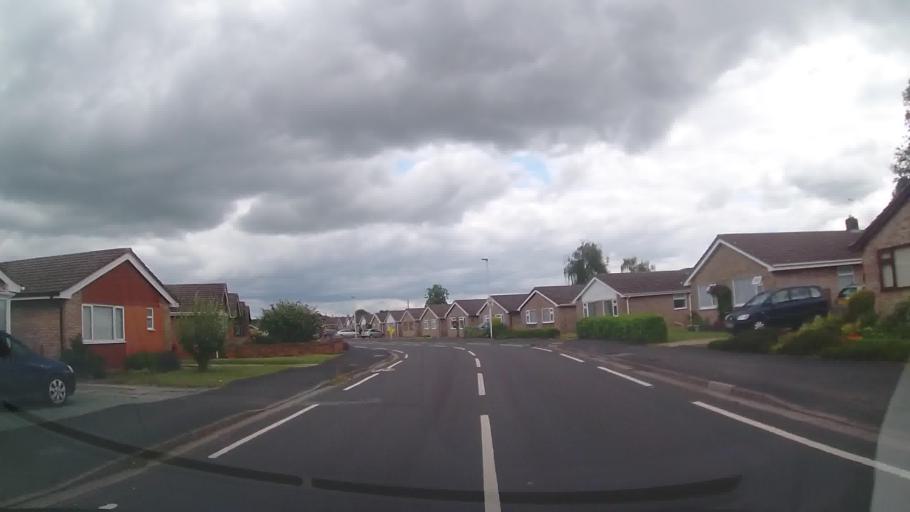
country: GB
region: England
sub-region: Shropshire
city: Wem
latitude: 52.8590
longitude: -2.7299
